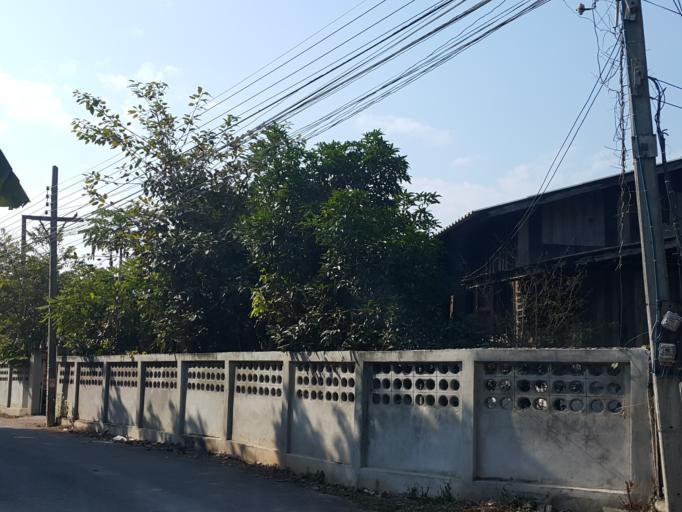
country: TH
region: Chiang Mai
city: San Sai
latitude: 18.8456
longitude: 99.1011
